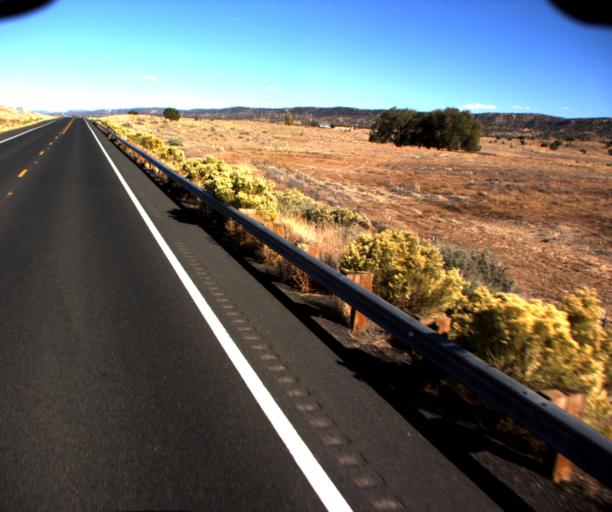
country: US
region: Arizona
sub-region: Coconino County
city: Kaibito
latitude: 36.4551
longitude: -110.7065
